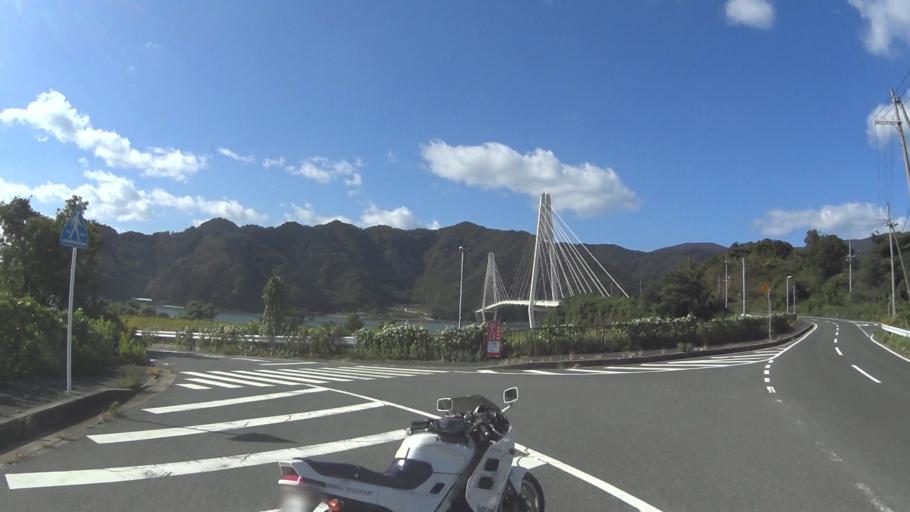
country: JP
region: Kyoto
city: Maizuru
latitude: 35.5073
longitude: 135.3933
